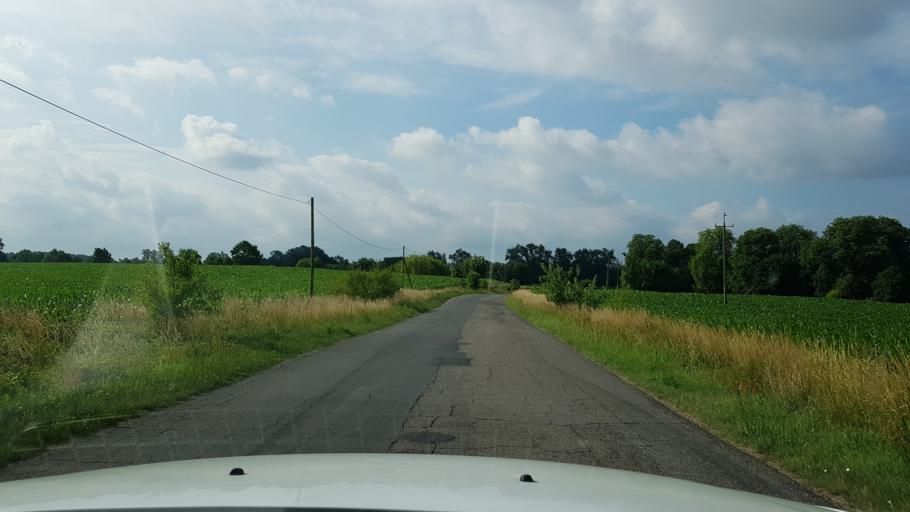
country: PL
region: West Pomeranian Voivodeship
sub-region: Powiat gryfinski
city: Gryfino
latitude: 53.2246
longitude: 14.5563
